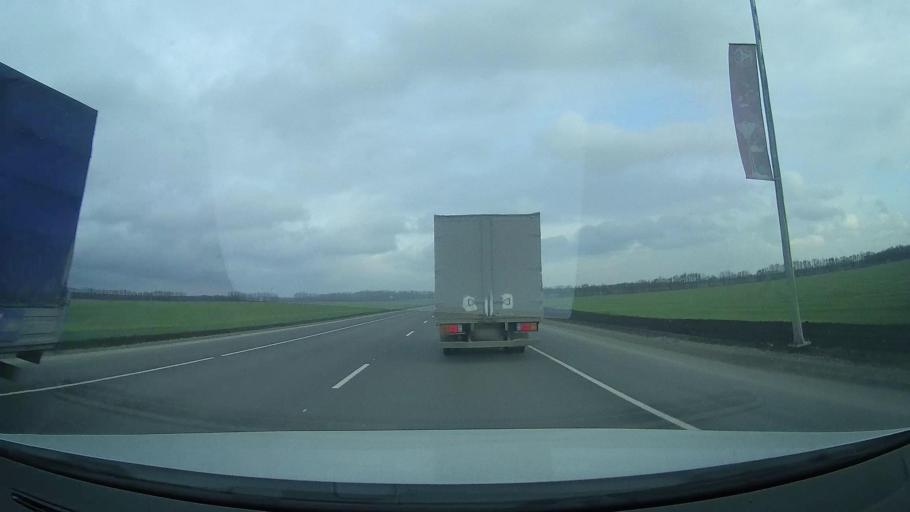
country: RU
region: Rostov
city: Grushevskaya
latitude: 47.4681
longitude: 39.8984
